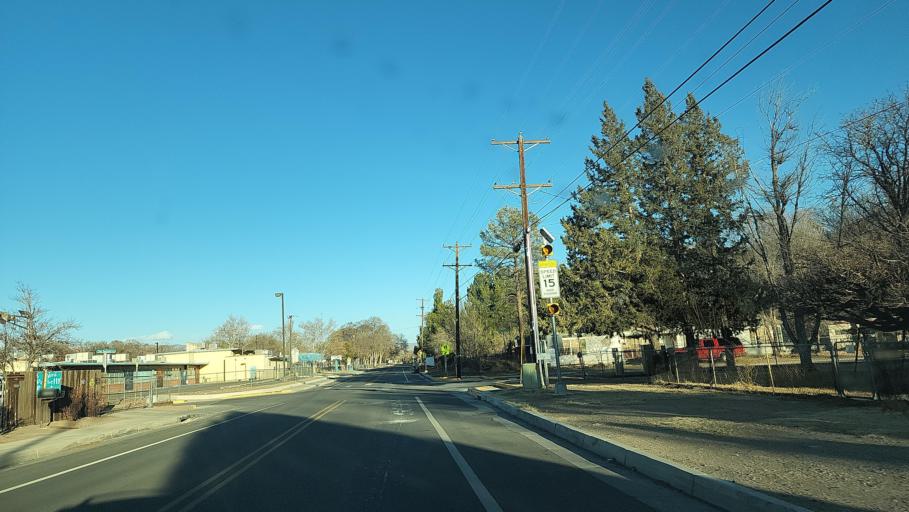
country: US
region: New Mexico
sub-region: Bernalillo County
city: South Valley
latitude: 35.0306
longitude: -106.6946
